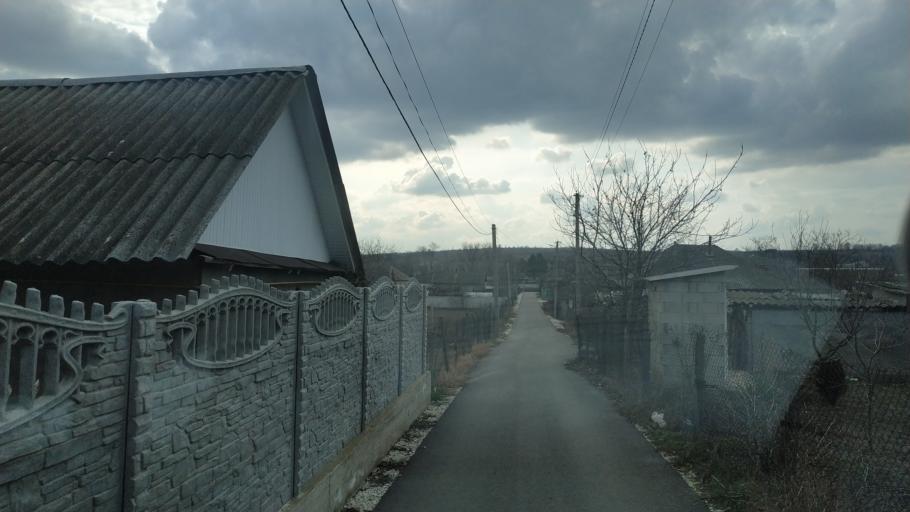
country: MD
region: Anenii Noi
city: Anenii Noi
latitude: 46.8999
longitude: 29.1423
